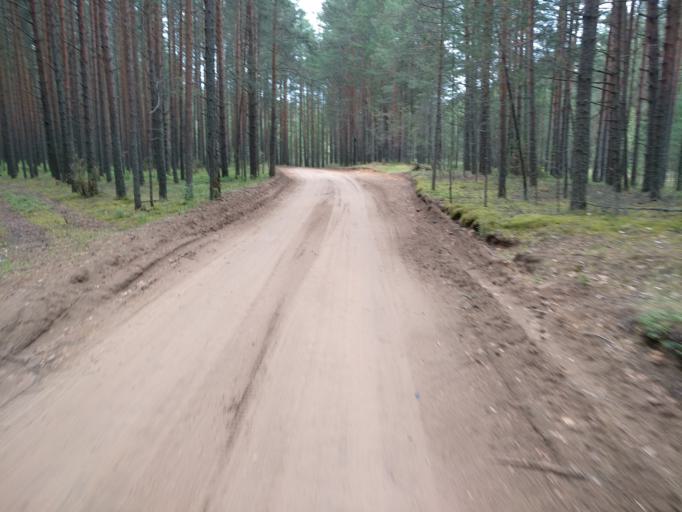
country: RU
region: Tverskaya
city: Krasnomayskiy
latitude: 57.5101
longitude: 34.4543
